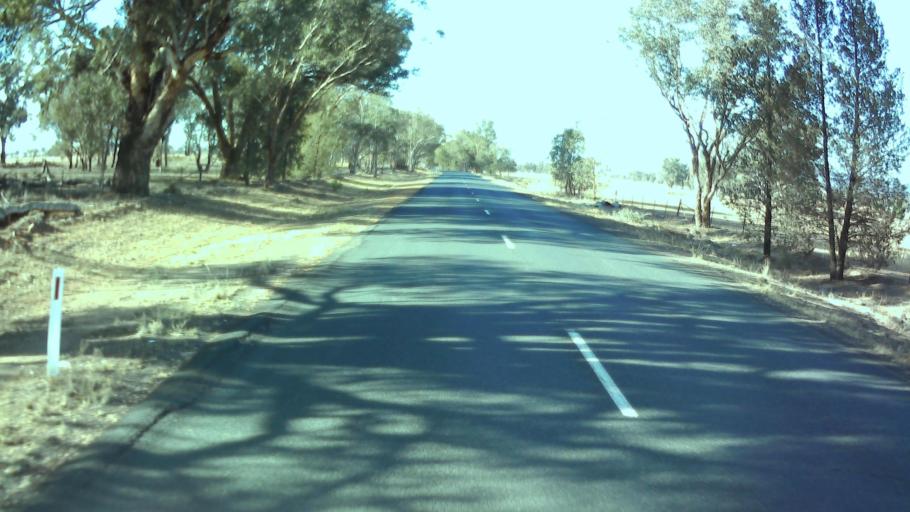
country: AU
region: New South Wales
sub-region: Weddin
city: Grenfell
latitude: -33.9272
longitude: 148.1380
